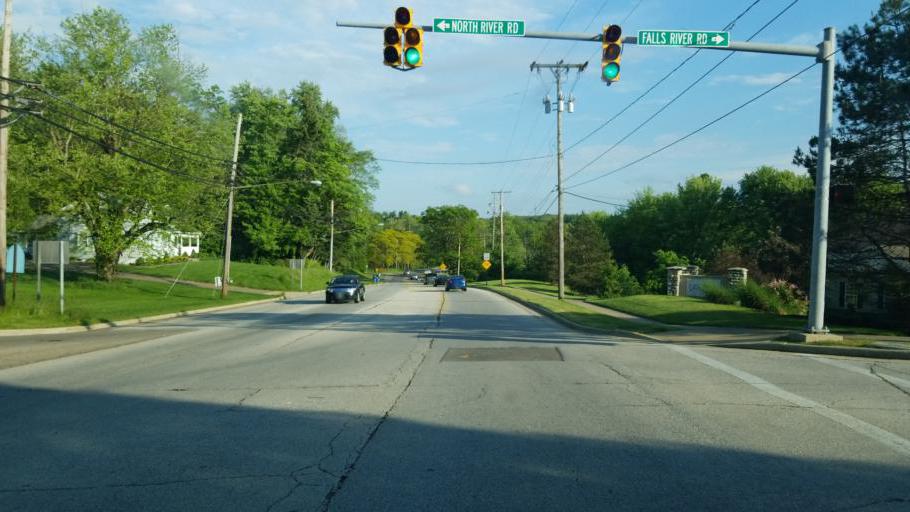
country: US
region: Ohio
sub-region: Summit County
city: Munroe Falls
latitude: 41.1448
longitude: -81.4401
